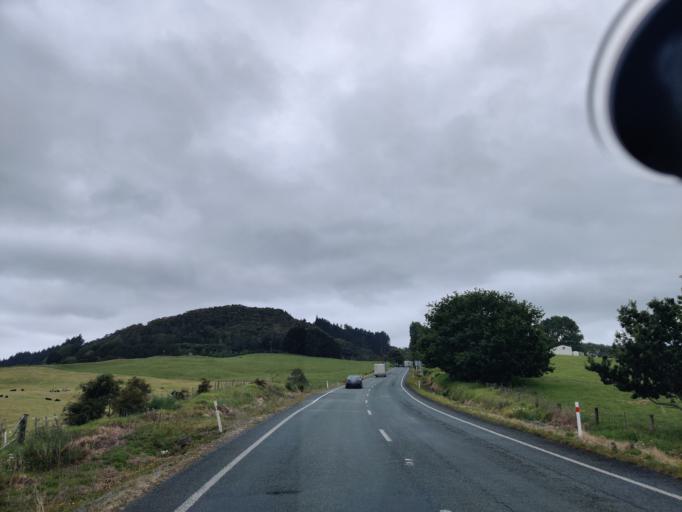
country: NZ
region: Northland
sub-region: Whangarei
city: Ruakaka
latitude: -36.0981
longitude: 174.4237
